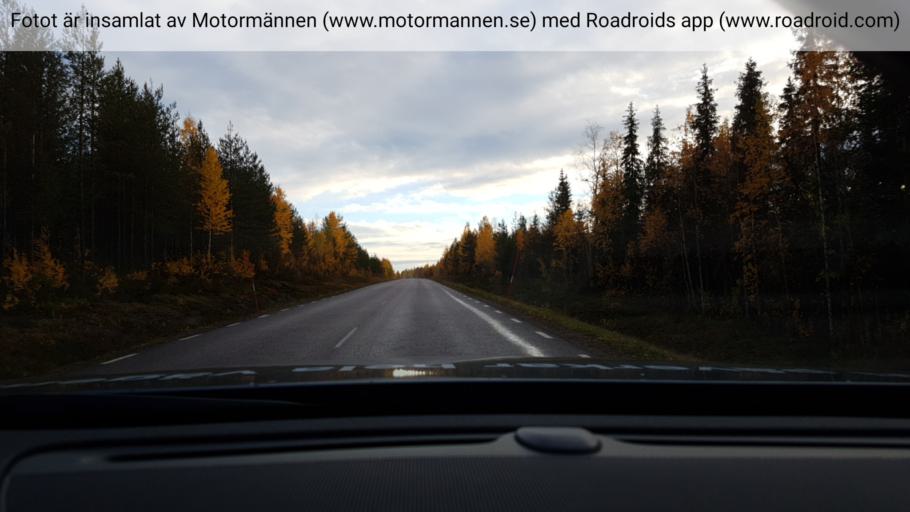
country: SE
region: Norrbotten
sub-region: Overkalix Kommun
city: OEverkalix
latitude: 66.8446
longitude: 22.7575
